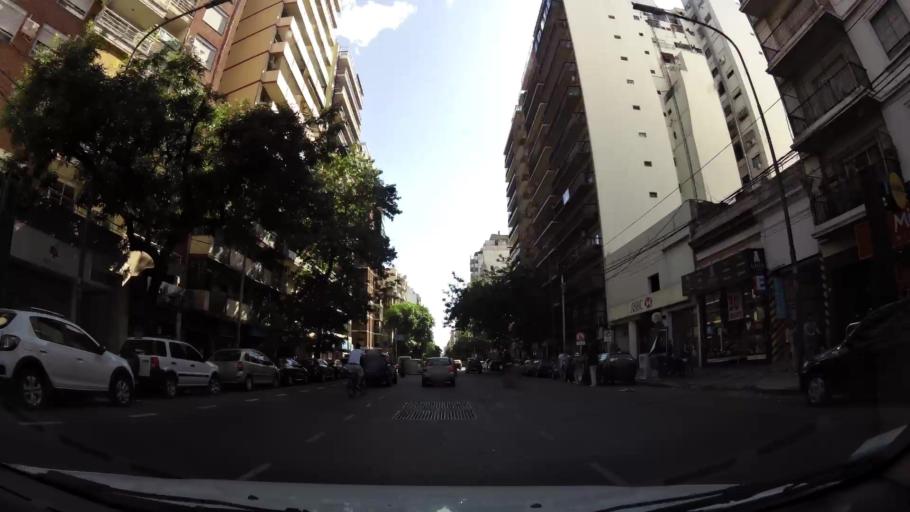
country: AR
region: Buenos Aires F.D.
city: Buenos Aires
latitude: -34.6119
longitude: -58.4218
